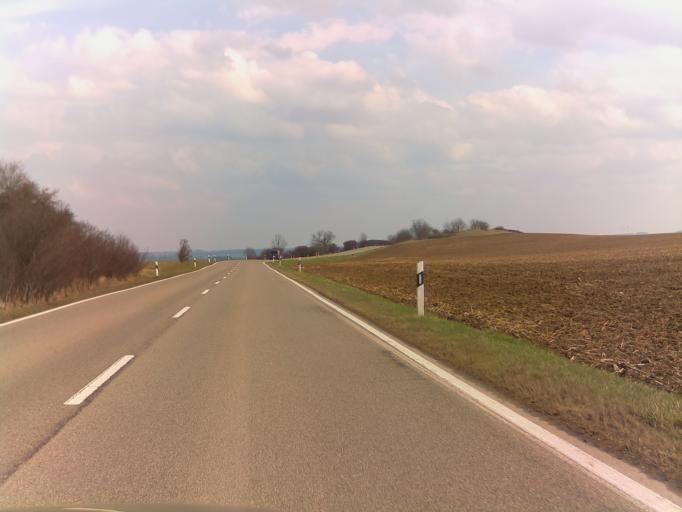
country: DE
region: Saxony-Anhalt
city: Eckartsberga
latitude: 51.1197
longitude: 11.5784
